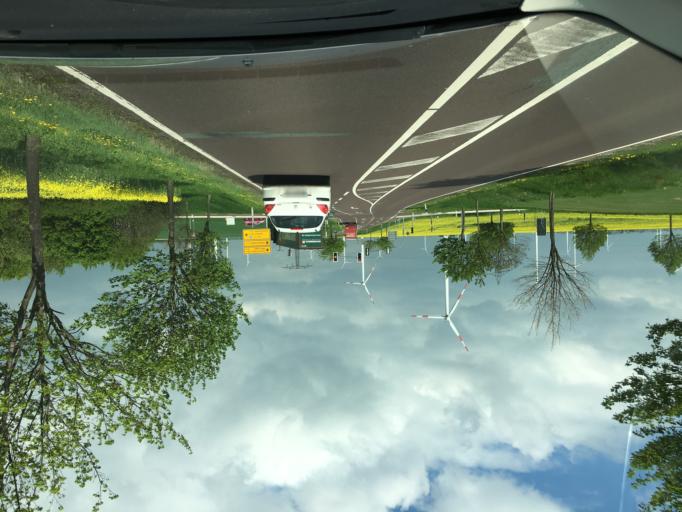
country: DE
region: Saxony-Anhalt
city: Sandersleben
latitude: 51.7223
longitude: 11.5856
